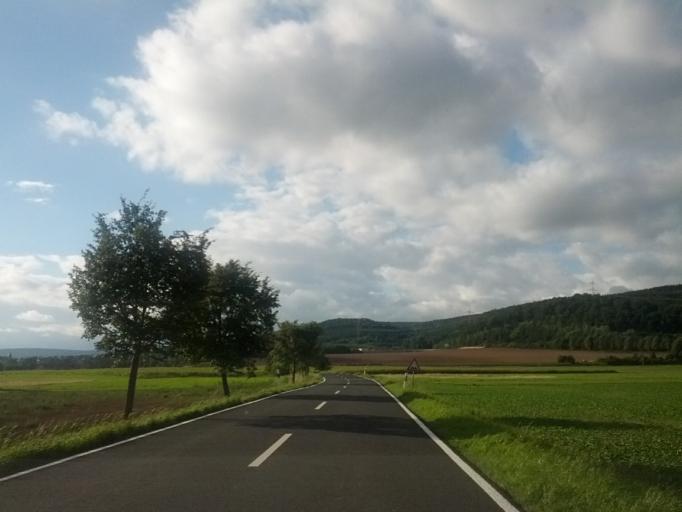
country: DE
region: Hesse
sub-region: Regierungsbezirk Kassel
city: Herleshausen
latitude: 50.9986
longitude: 10.1936
